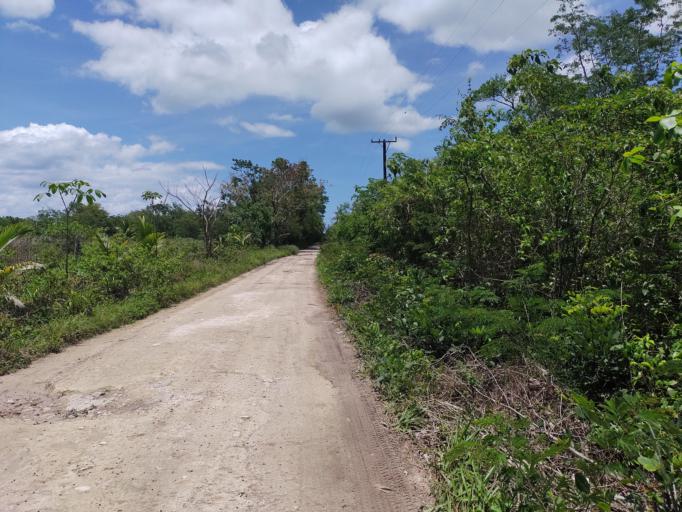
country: MX
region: Quintana Roo
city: San Miguel de Cozumel
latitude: 20.4974
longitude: -86.9027
